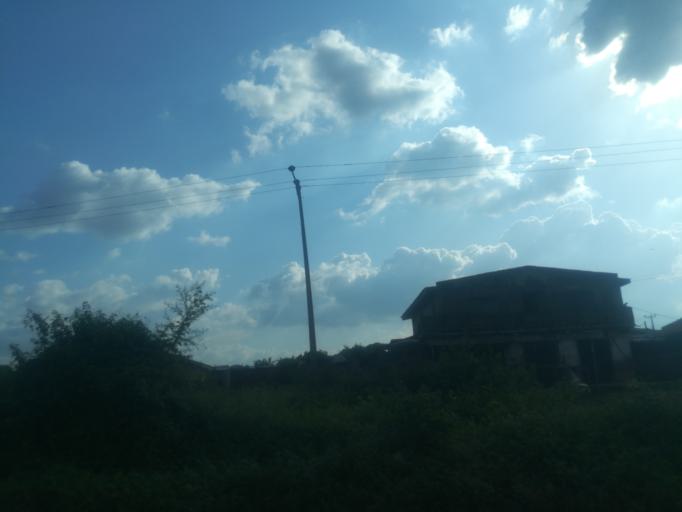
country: NG
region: Oyo
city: Egbeda
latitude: 7.3882
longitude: 3.9785
